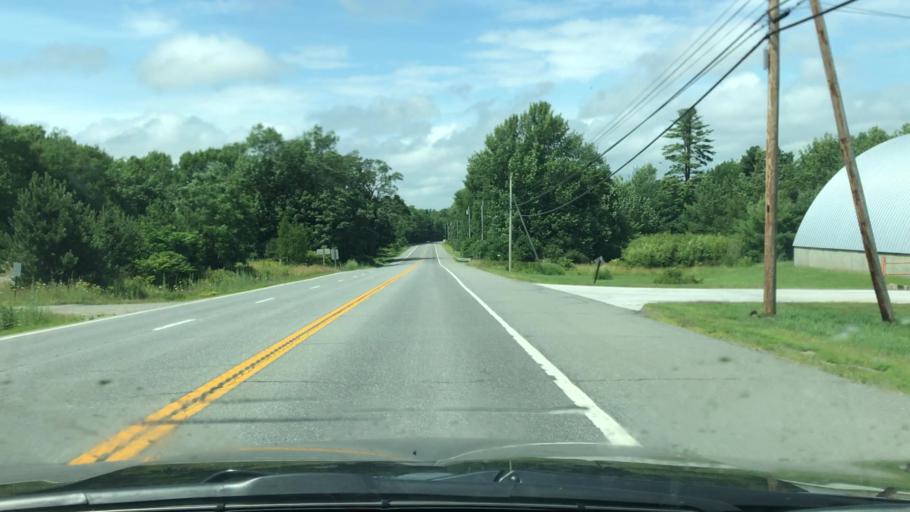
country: US
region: Maine
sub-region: Waldo County
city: Northport
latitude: 44.3670
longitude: -68.9799
